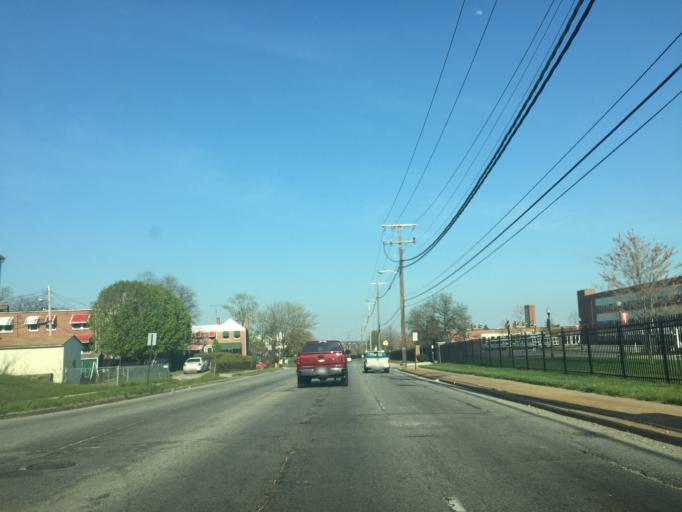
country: US
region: Maryland
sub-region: City of Baltimore
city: Baltimore
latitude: 39.3136
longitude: -76.5666
